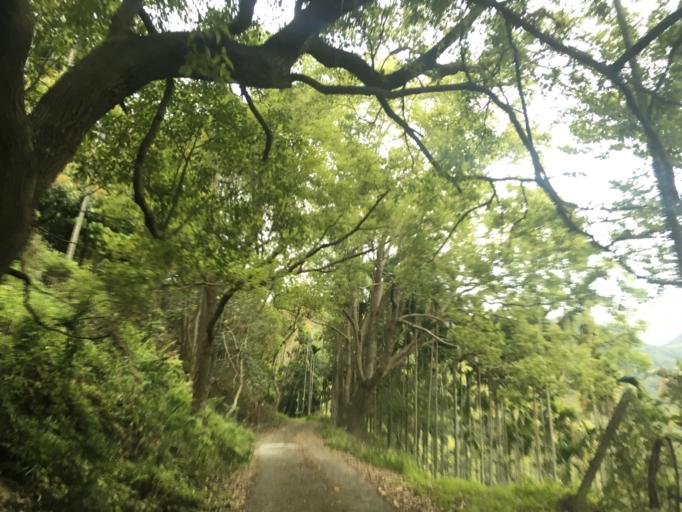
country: TW
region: Taiwan
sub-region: Taichung City
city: Taichung
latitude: 24.1355
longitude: 120.8210
